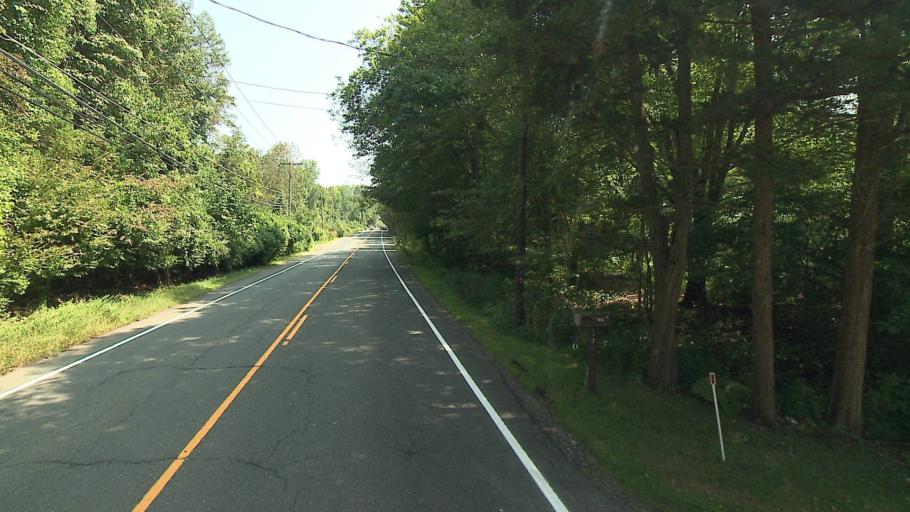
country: US
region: Connecticut
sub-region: Fairfield County
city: Georgetown
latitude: 41.2695
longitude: -73.4492
